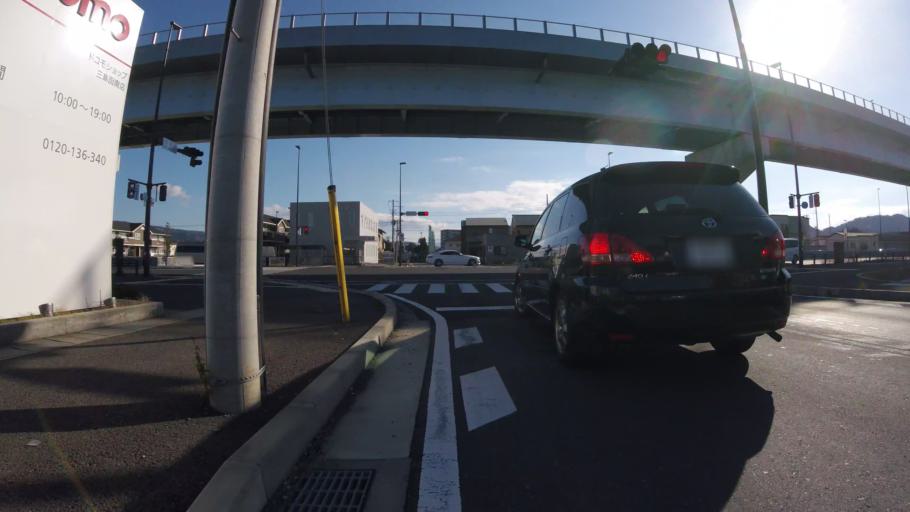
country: JP
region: Shizuoka
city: Mishima
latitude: 35.0829
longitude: 138.9352
